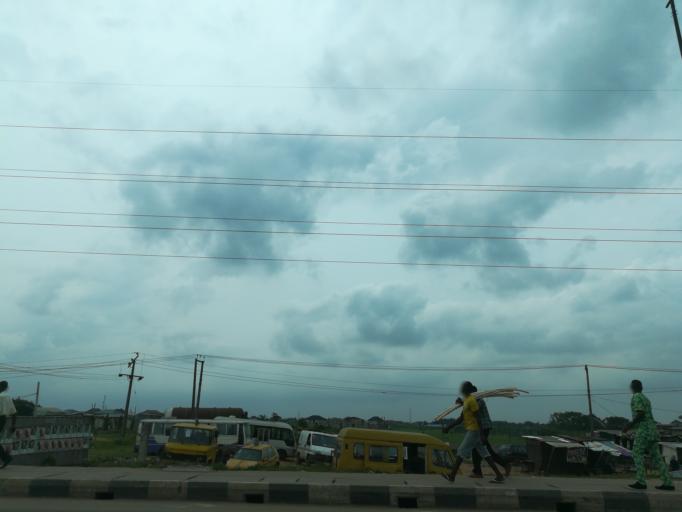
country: NG
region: Lagos
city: Ojota
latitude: 6.6050
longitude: 3.4063
